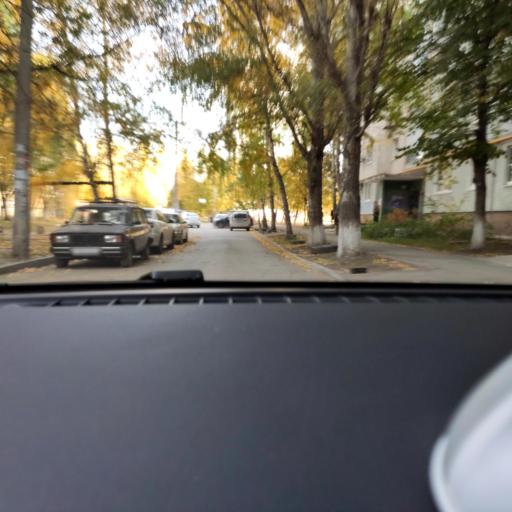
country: RU
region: Samara
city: Samara
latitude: 53.2649
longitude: 50.2228
